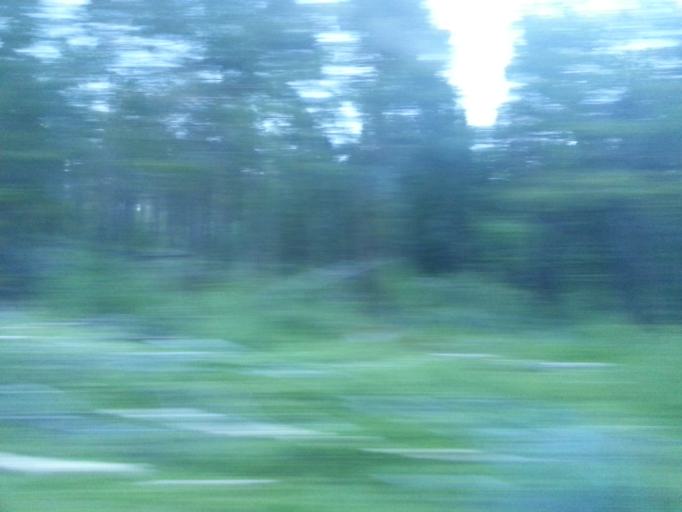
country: NO
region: Oppland
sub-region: Dovre
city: Dombas
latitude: 62.0885
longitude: 9.1445
